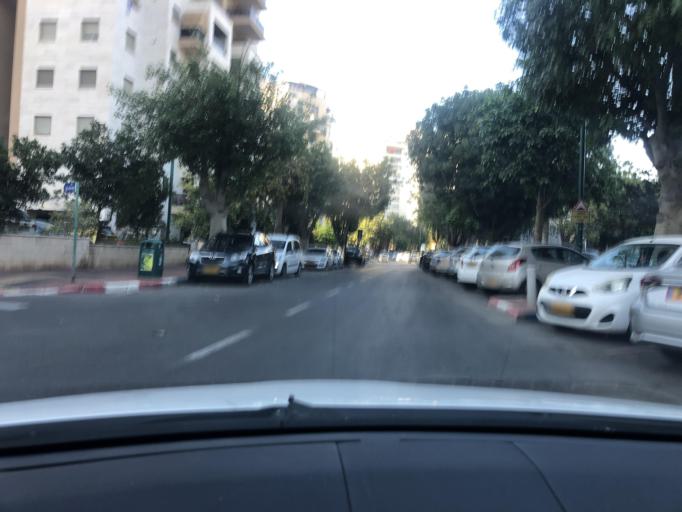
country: IL
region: Tel Aviv
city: Bene Beraq
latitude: 32.0615
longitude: 34.8350
